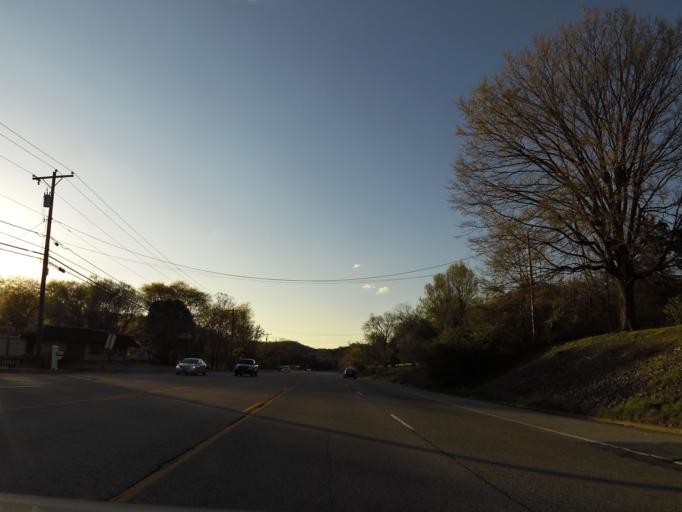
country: US
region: Tennessee
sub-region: Sumner County
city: Millersville
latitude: 36.3715
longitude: -86.7426
